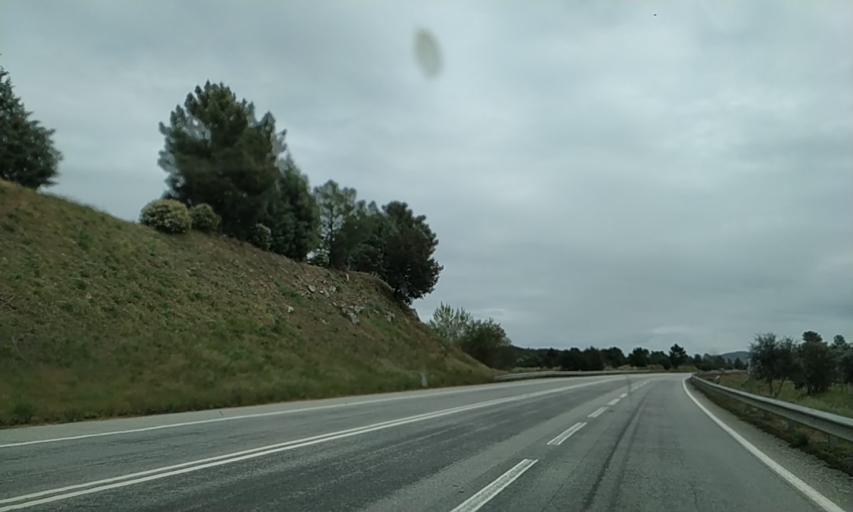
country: PT
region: Guarda
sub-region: Celorico da Beira
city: Celorico da Beira
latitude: 40.6349
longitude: -7.3179
